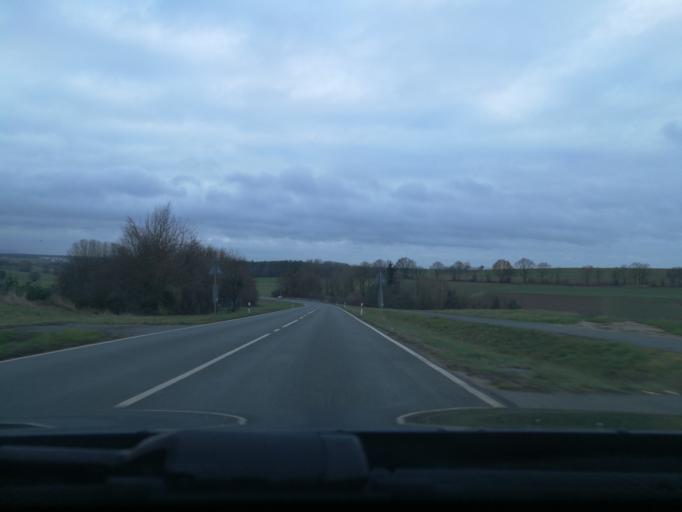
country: DE
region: Bavaria
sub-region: Regierungsbezirk Mittelfranken
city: Kalchreuth
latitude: 49.5560
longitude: 11.1401
